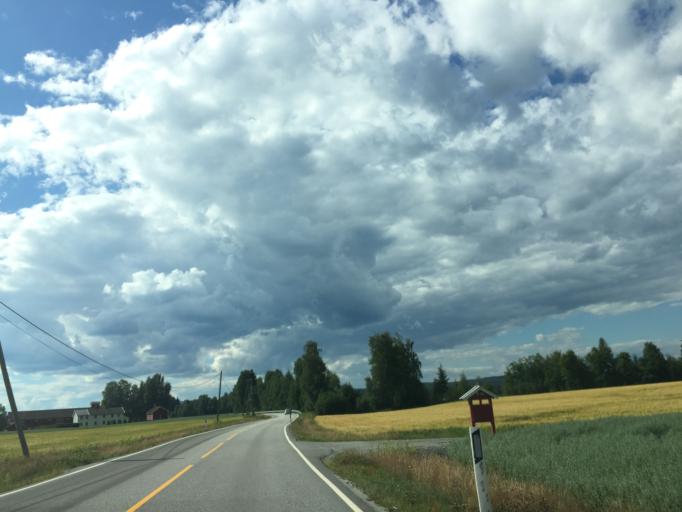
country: NO
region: Hedmark
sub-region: Sor-Odal
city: Skarnes
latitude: 60.2369
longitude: 11.7728
